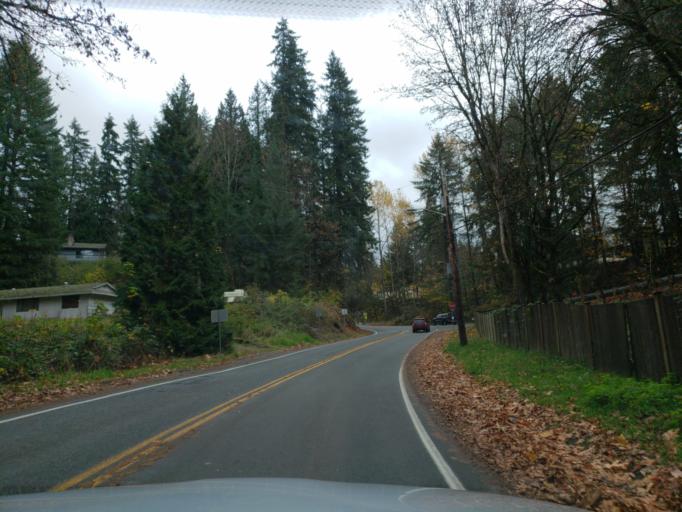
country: US
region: Washington
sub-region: King County
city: Woodinville
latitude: 47.7531
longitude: -122.1412
